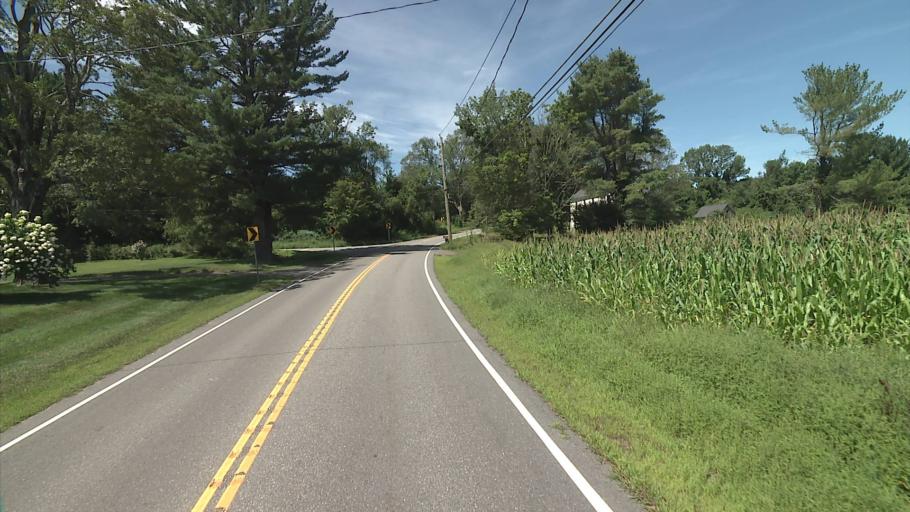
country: US
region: Connecticut
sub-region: Windham County
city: South Woodstock
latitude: 41.8952
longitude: -71.9907
